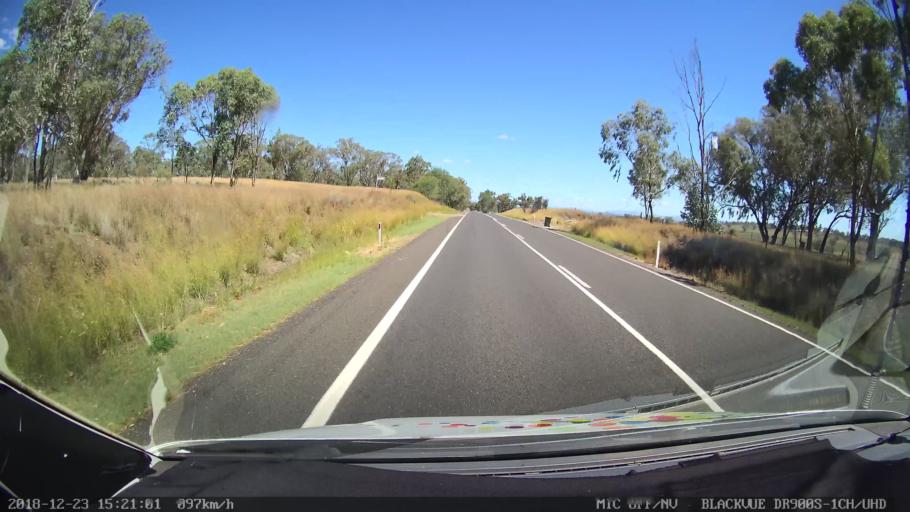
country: AU
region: New South Wales
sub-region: Tamworth Municipality
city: Manilla
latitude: -30.8506
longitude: 150.7937
